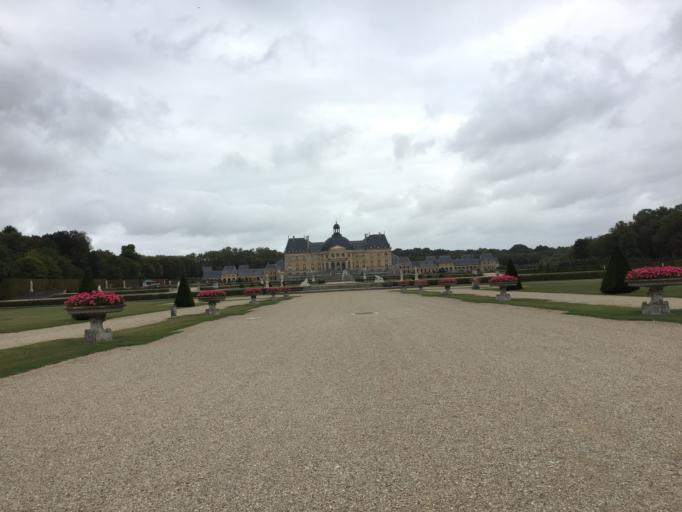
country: FR
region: Ile-de-France
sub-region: Departement de Seine-et-Marne
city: Maincy
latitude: 48.5624
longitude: 2.7147
